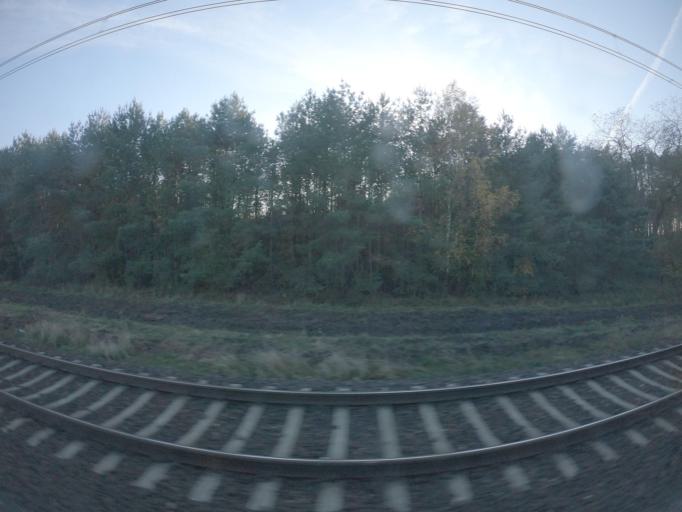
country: PL
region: Lubusz
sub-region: Powiat slubicki
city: Rzepin
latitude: 52.2733
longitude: 14.9195
